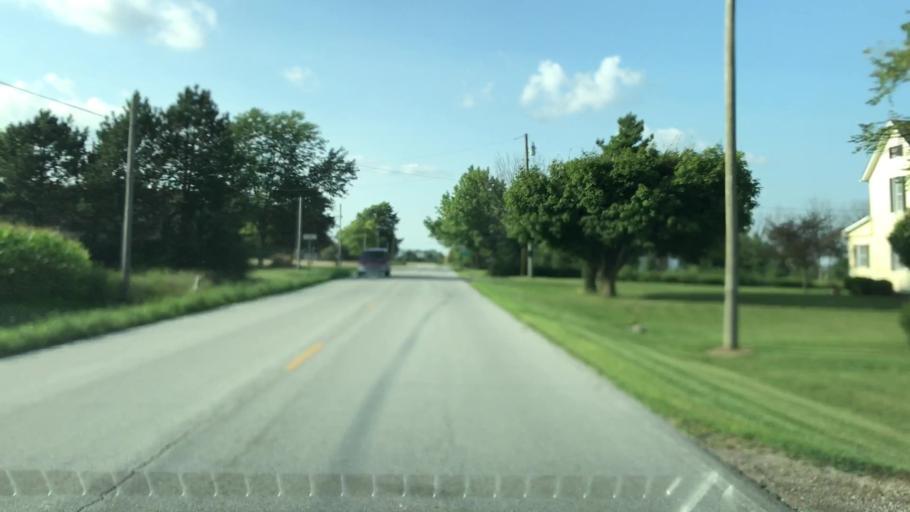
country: US
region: Ohio
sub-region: Union County
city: Marysville
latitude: 40.2120
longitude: -83.3542
